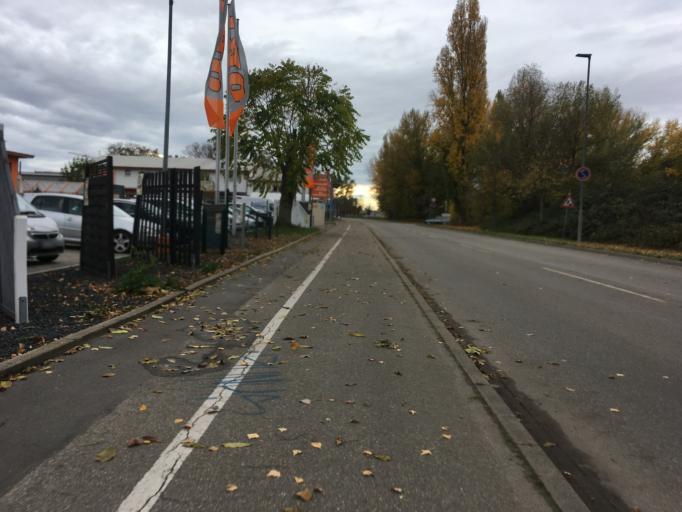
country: DE
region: Baden-Wuerttemberg
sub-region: Freiburg Region
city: Breisach am Rhein
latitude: 48.0396
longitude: 7.5723
